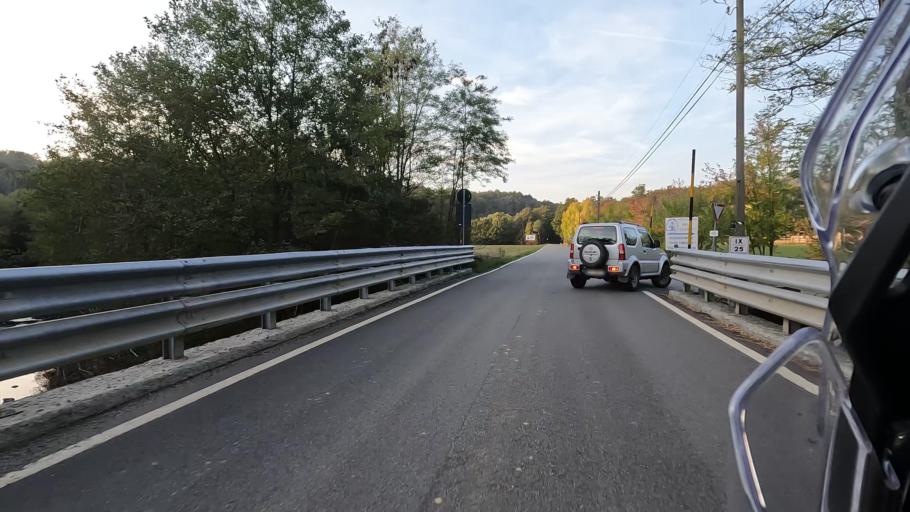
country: IT
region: Liguria
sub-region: Provincia di Savona
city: Sassello
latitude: 44.5034
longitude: 8.4839
